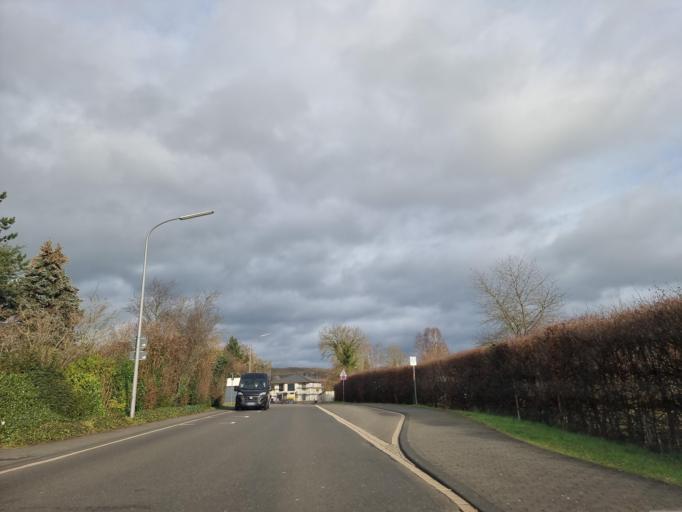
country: DE
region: Rheinland-Pfalz
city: Neuerburg
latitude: 49.9976
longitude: 6.9413
